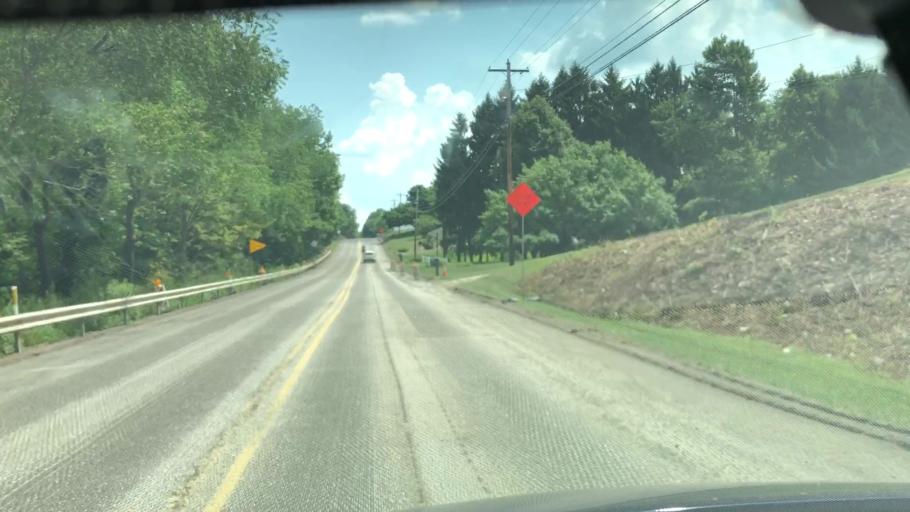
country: US
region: Pennsylvania
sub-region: Butler County
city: Saxonburg
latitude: 40.7907
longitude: -79.8082
